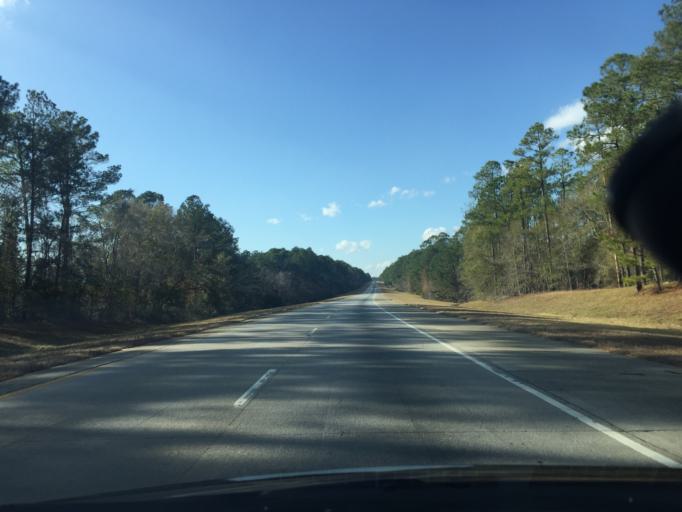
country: US
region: Georgia
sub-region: Treutlen County
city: Soperton
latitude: 32.4282
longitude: -82.4761
